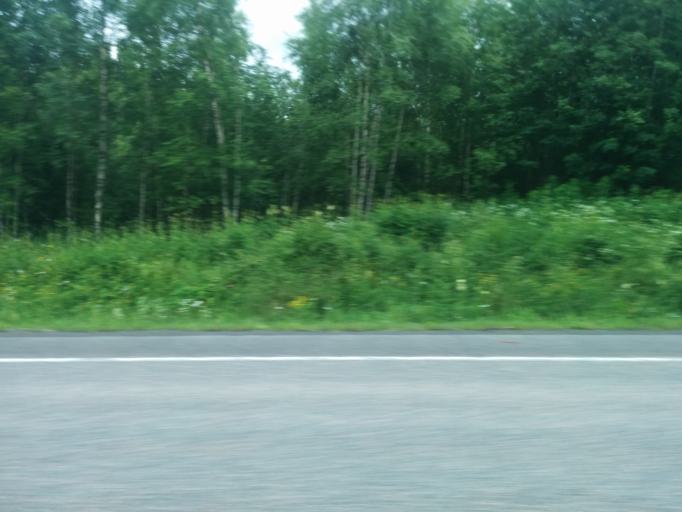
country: FI
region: Pirkanmaa
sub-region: Tampere
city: Orivesi
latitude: 61.7047
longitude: 24.4449
